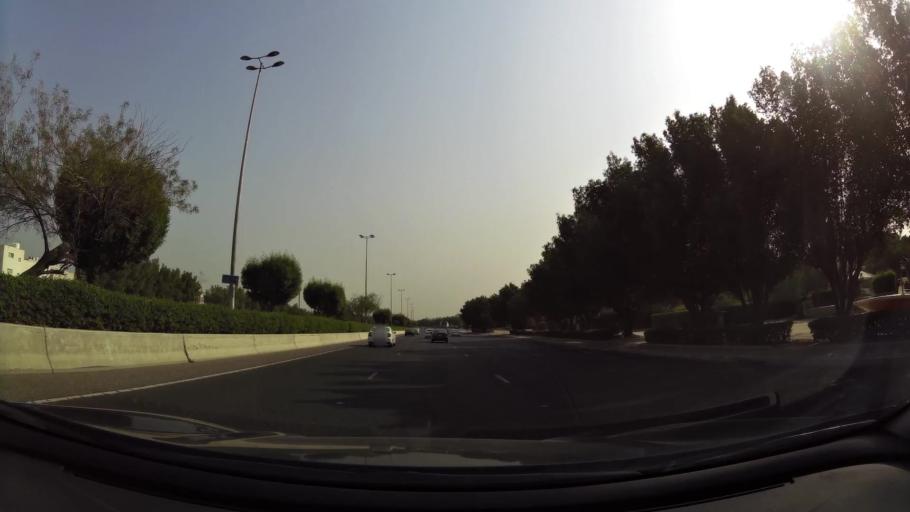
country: KW
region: Mubarak al Kabir
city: Sabah as Salim
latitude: 29.2400
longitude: 48.0708
